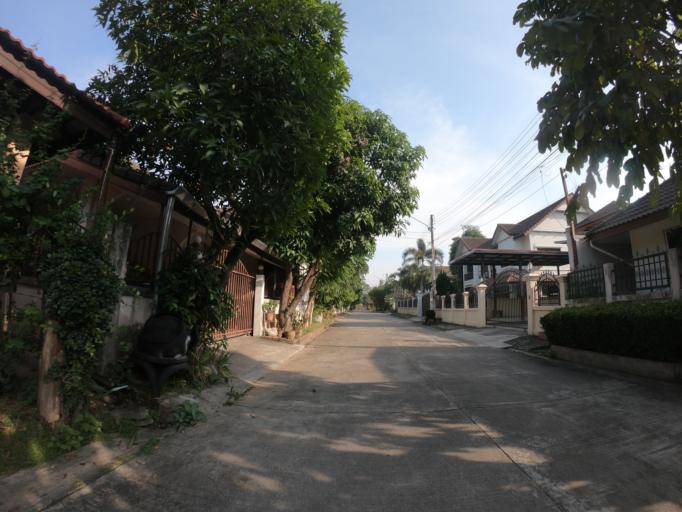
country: TH
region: Chiang Mai
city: Chiang Mai
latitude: 18.8184
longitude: 99.0150
